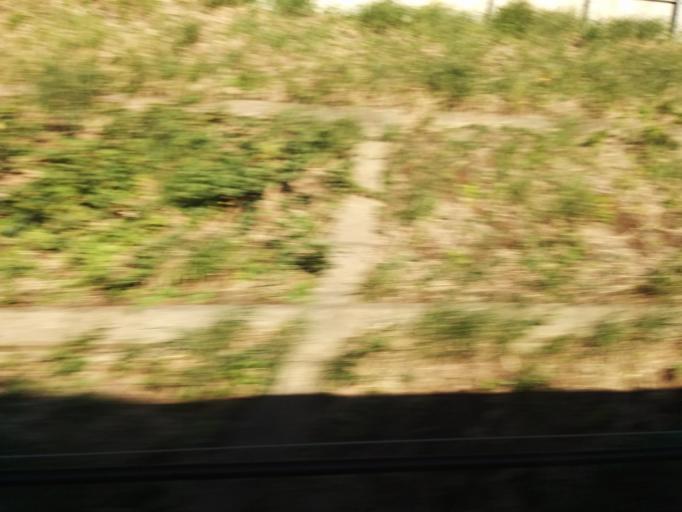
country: JP
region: Kanagawa
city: Minami-rinkan
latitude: 35.4234
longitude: 139.4454
